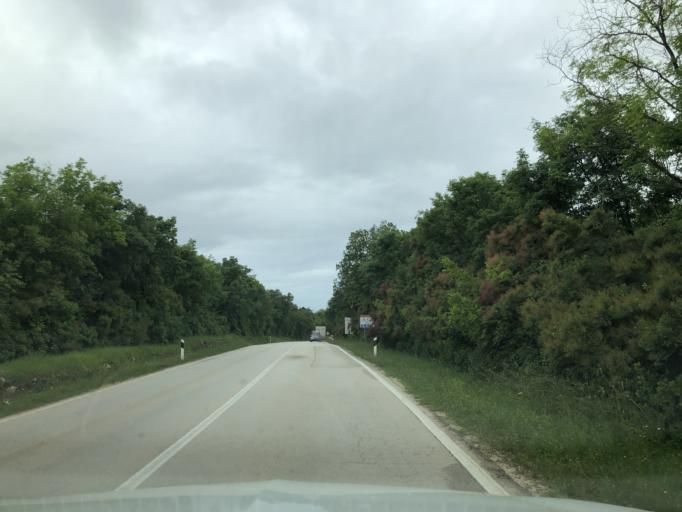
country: SI
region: Piran-Pirano
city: Seca
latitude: 45.4583
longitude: 13.6071
